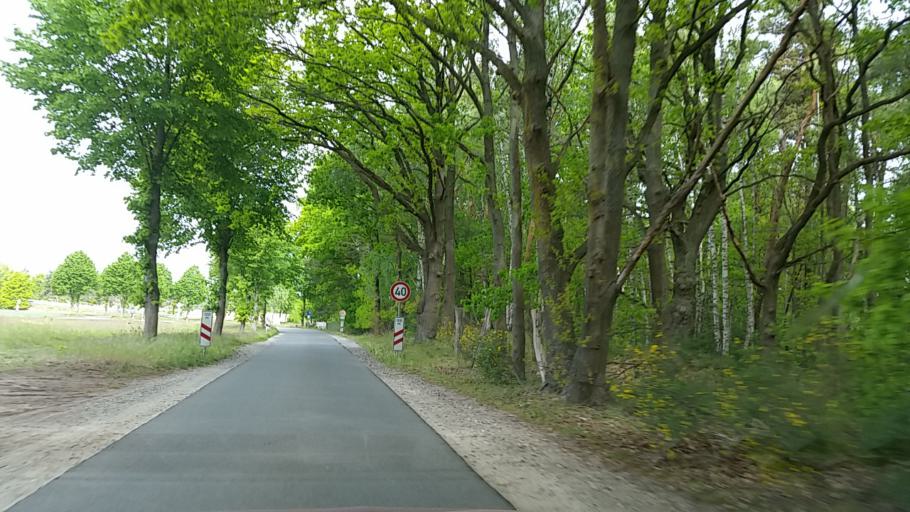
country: DE
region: Lower Saxony
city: Wieren
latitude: 52.8633
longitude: 10.6682
